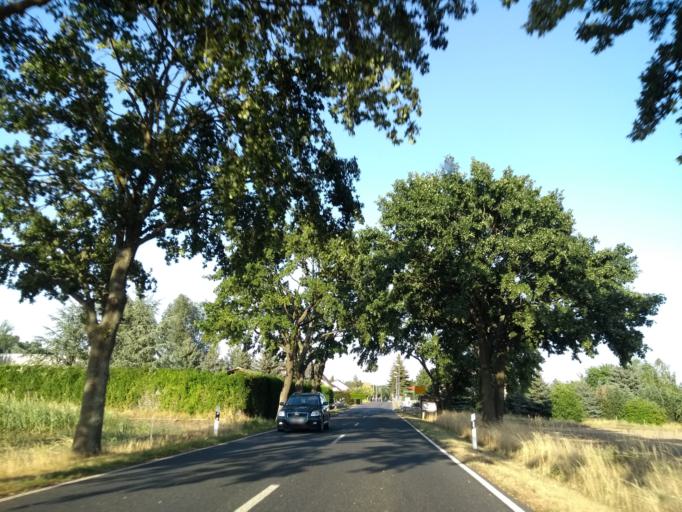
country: DE
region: Brandenburg
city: Lubbenau
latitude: 51.8470
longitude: 13.8934
